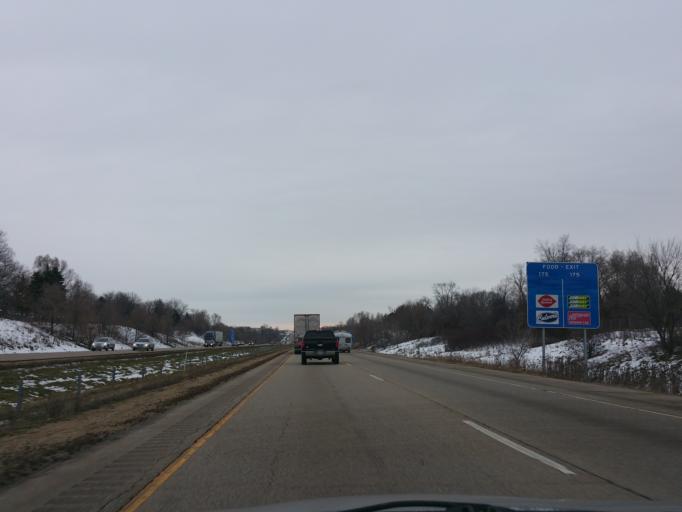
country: US
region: Wisconsin
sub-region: Rock County
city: Janesville
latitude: 42.6902
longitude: -88.9839
